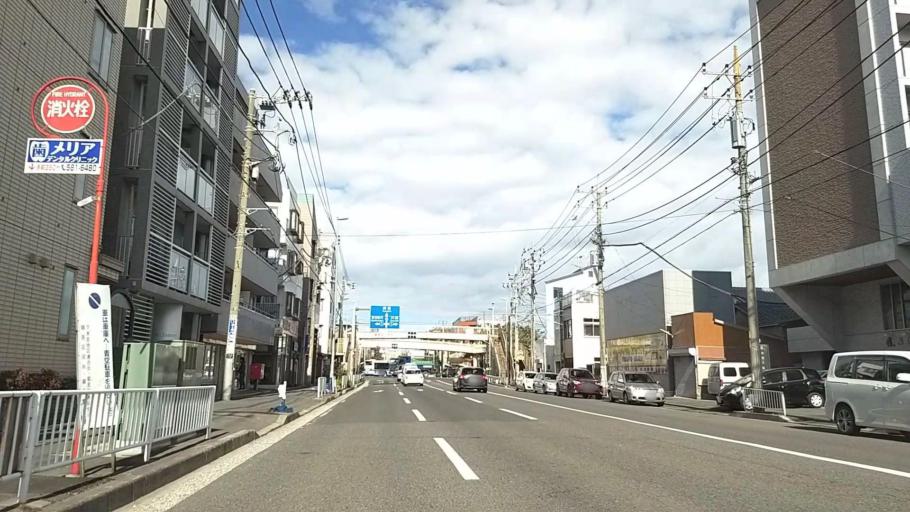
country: JP
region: Kanagawa
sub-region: Kawasaki-shi
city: Kawasaki
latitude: 35.5204
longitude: 139.6723
